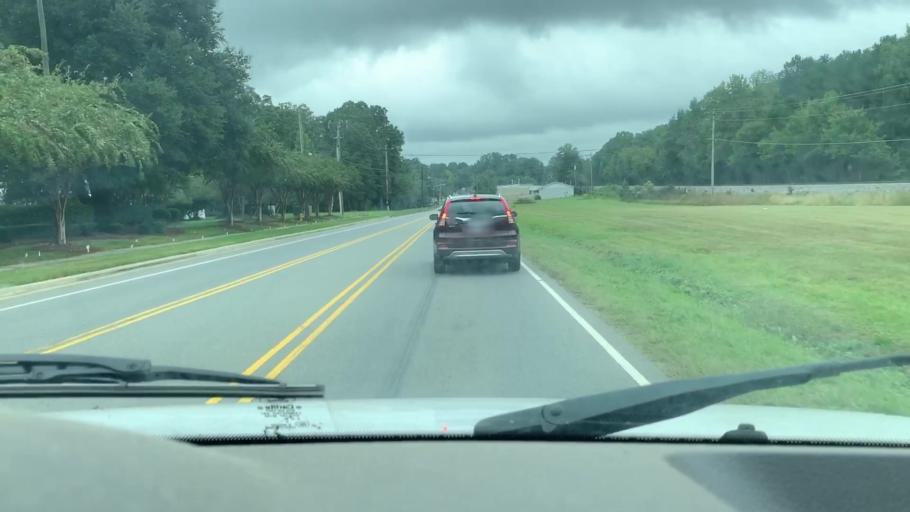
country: US
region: North Carolina
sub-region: Mecklenburg County
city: Huntersville
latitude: 35.3993
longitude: -80.8384
